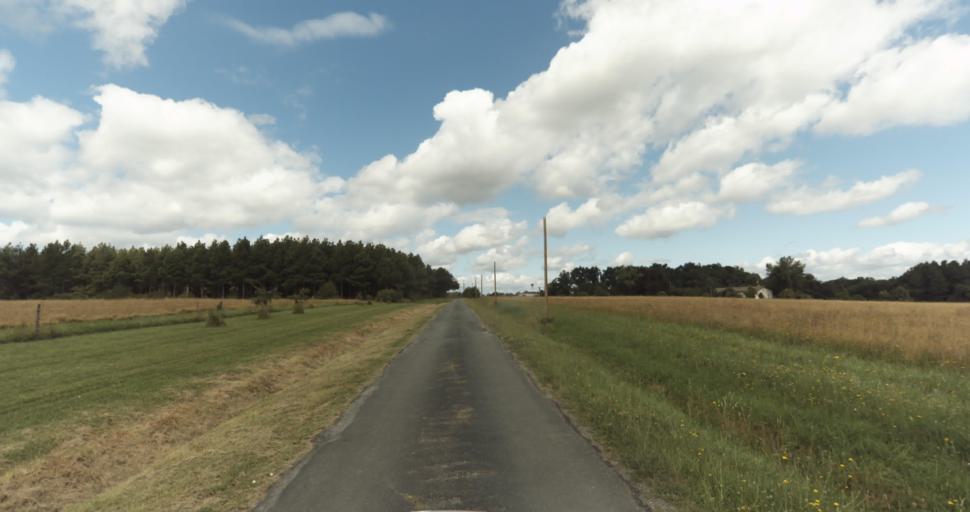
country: FR
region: Aquitaine
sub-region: Departement de la Gironde
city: Bazas
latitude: 44.4592
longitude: -0.1764
